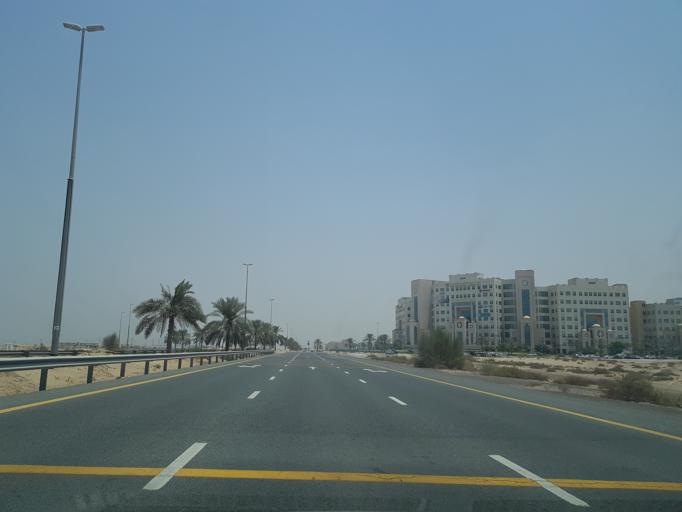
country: AE
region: Ash Shariqah
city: Sharjah
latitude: 25.1237
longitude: 55.4067
